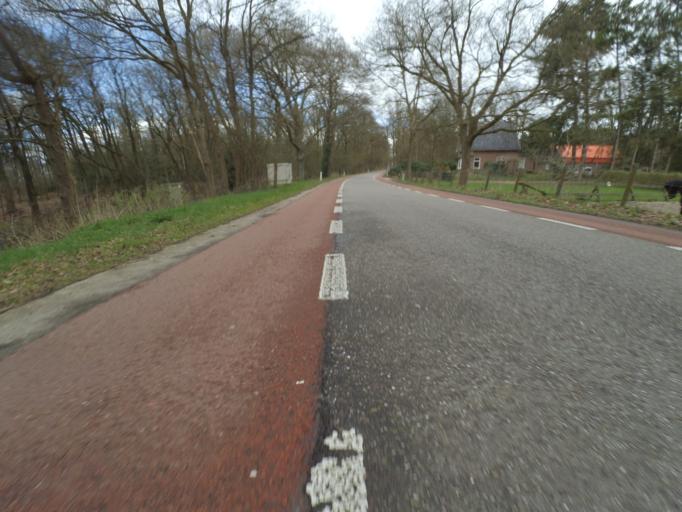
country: NL
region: Gelderland
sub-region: Gemeente Apeldoorn
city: Beekbergen
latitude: 52.1121
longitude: 5.8755
